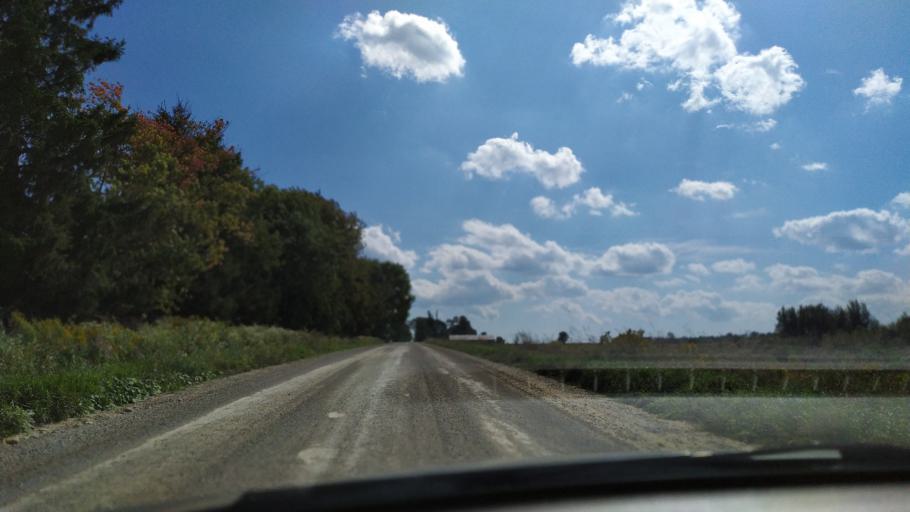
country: CA
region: Ontario
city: Stratford
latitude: 43.2887
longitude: -80.9307
